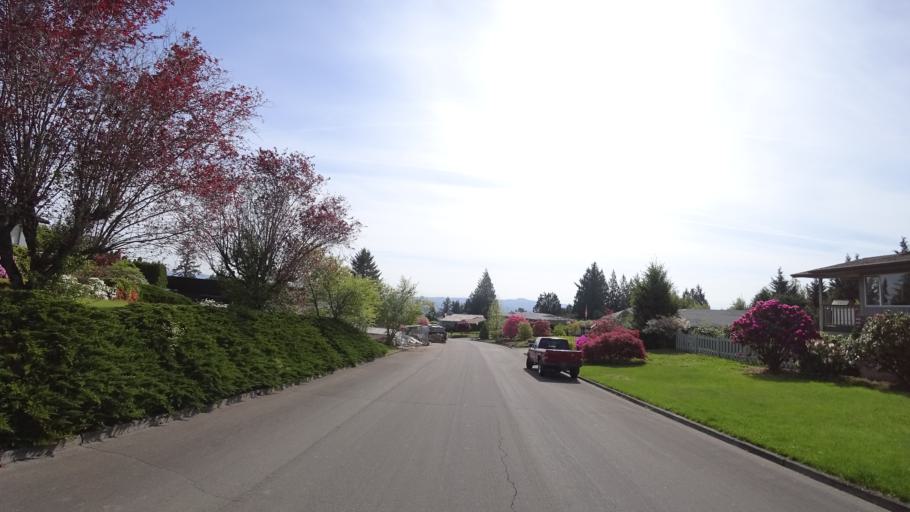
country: US
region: Oregon
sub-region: Washington County
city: Aloha
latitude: 45.4503
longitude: -122.8508
